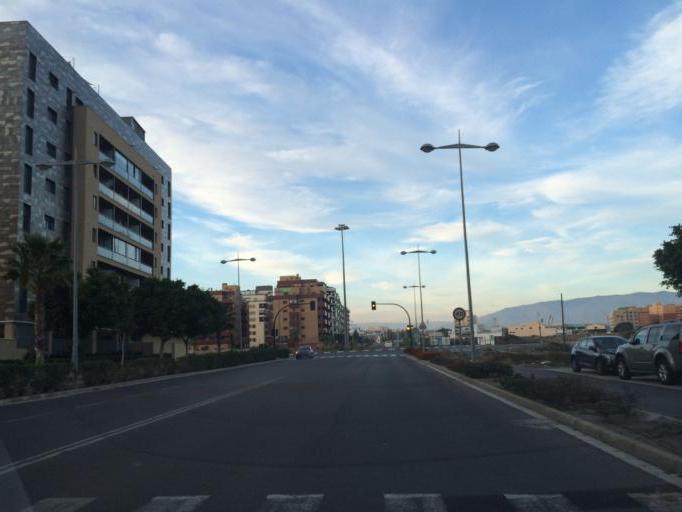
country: ES
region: Andalusia
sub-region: Provincia de Almeria
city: Almeria
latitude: 36.8314
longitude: -2.4381
